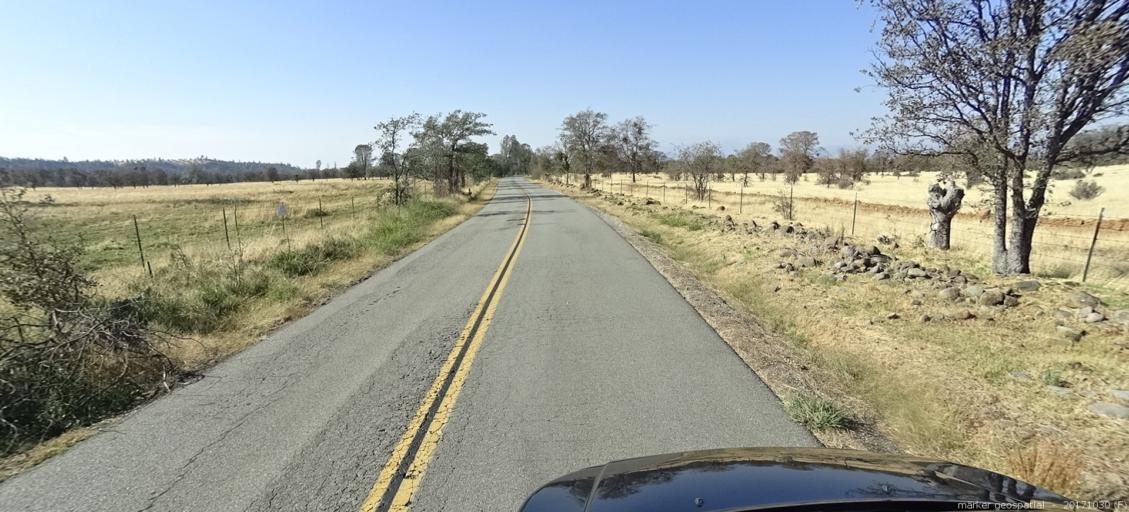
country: US
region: California
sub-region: Shasta County
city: Shingletown
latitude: 40.6358
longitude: -121.9712
